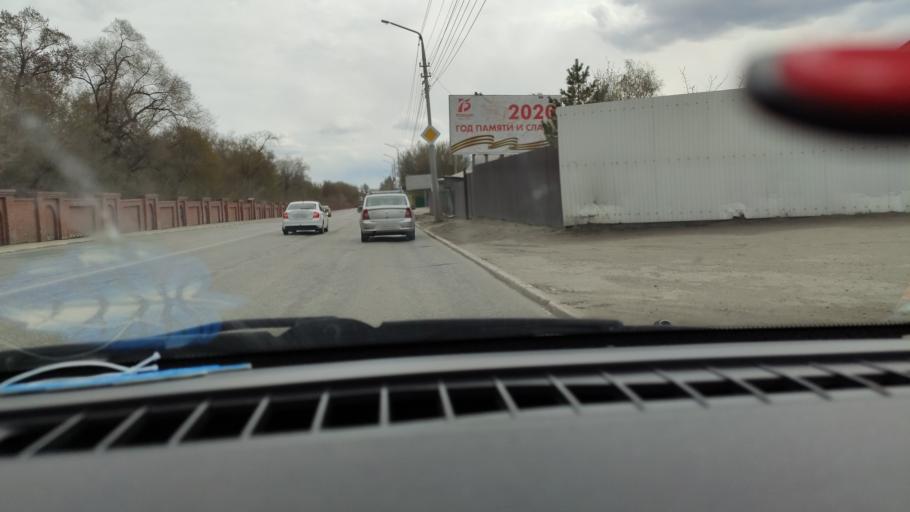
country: RU
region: Saratov
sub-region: Saratovskiy Rayon
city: Saratov
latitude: 51.5571
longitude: 46.0058
